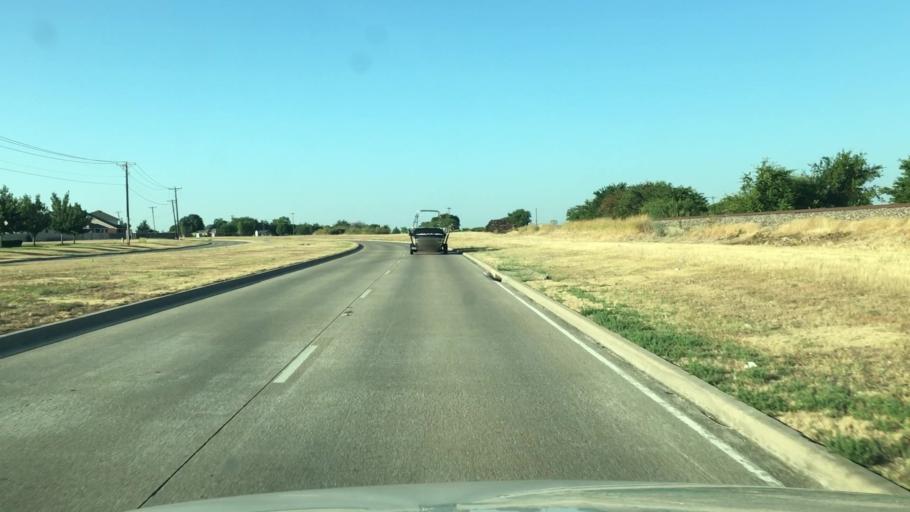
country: US
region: Texas
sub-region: Tarrant County
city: Crowley
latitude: 32.5469
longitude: -97.3657
